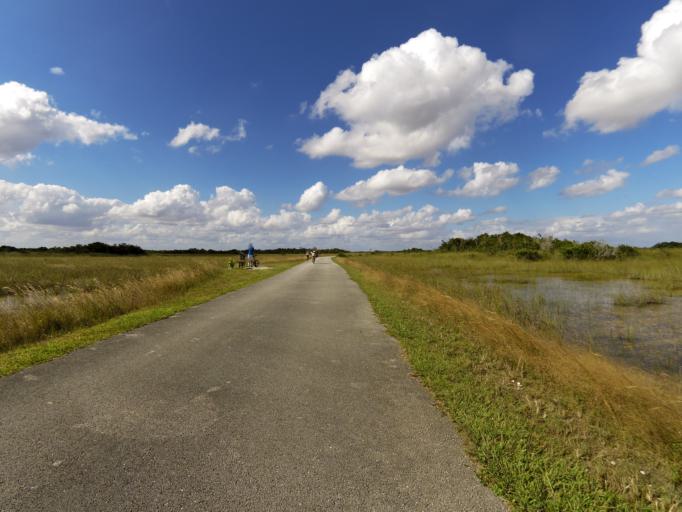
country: US
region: Florida
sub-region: Miami-Dade County
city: The Hammocks
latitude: 25.7058
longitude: -80.7613
